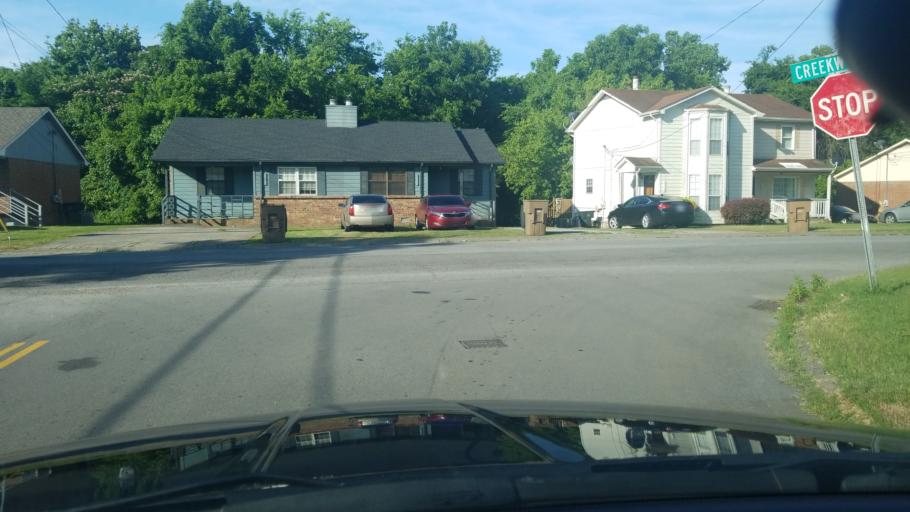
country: US
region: Tennessee
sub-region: Davidson County
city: Nashville
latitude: 36.2313
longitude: -86.7724
